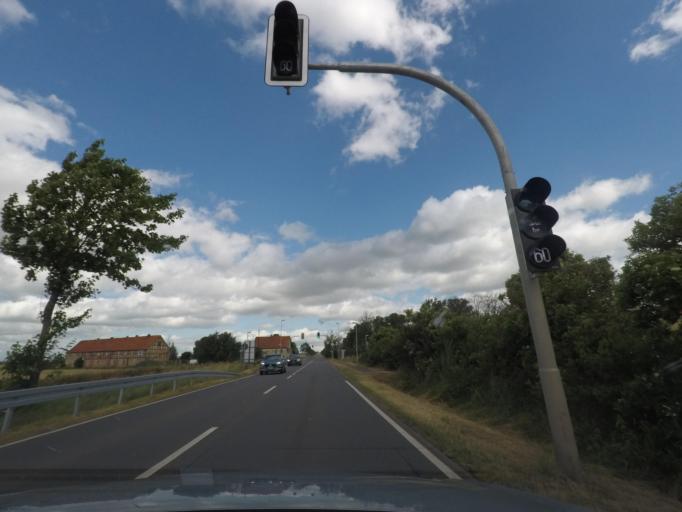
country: DE
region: Saxony-Anhalt
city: Harsleben
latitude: 51.8293
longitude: 11.1166
